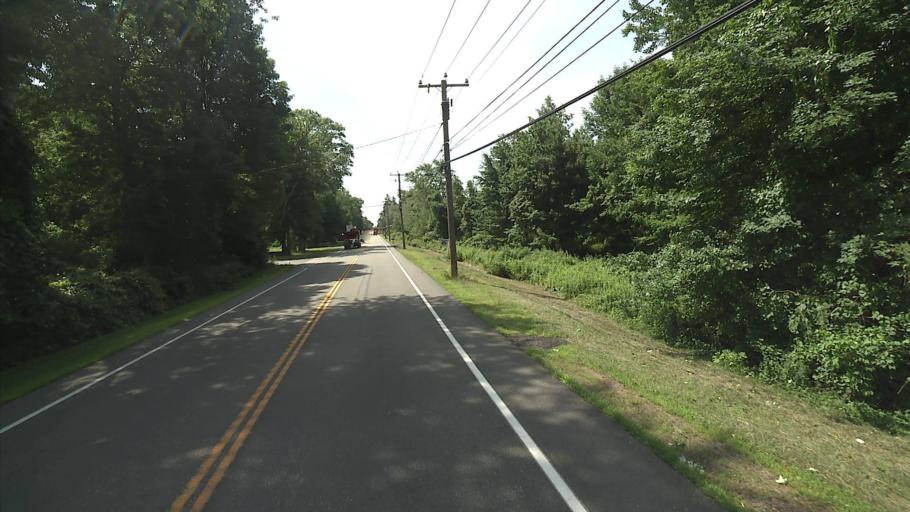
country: US
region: Connecticut
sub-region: Tolland County
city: Tolland
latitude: 41.8131
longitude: -72.3962
